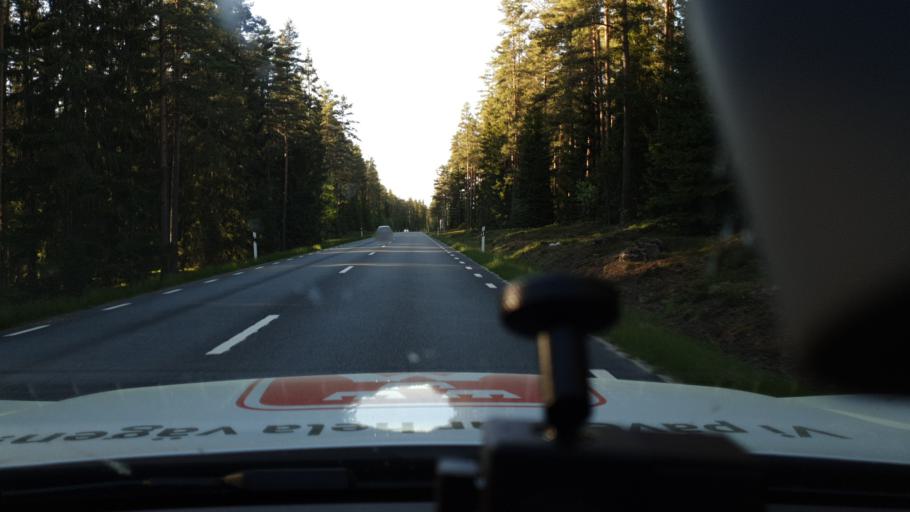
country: SE
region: Joenkoeping
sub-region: Eksjo Kommun
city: Eksjoe
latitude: 57.5833
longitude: 14.9699
